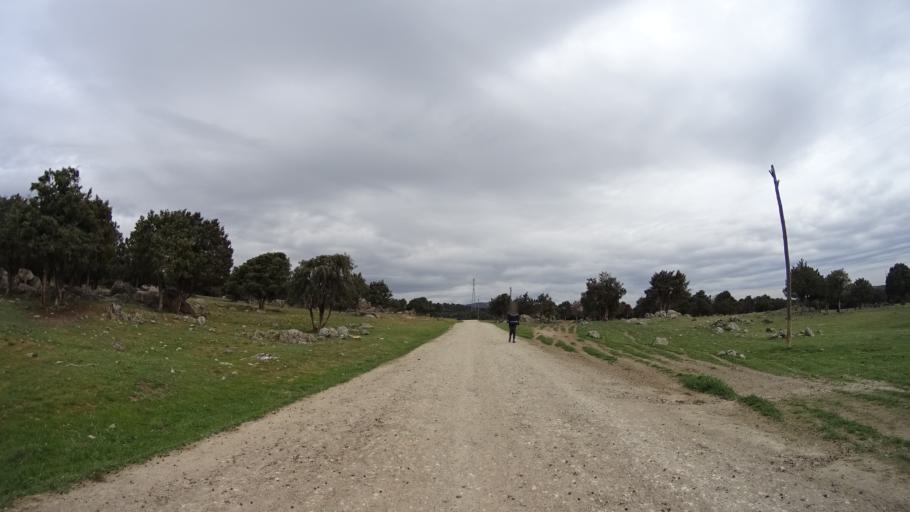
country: ES
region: Madrid
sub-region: Provincia de Madrid
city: Hoyo de Manzanares
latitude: 40.6079
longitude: -3.8773
